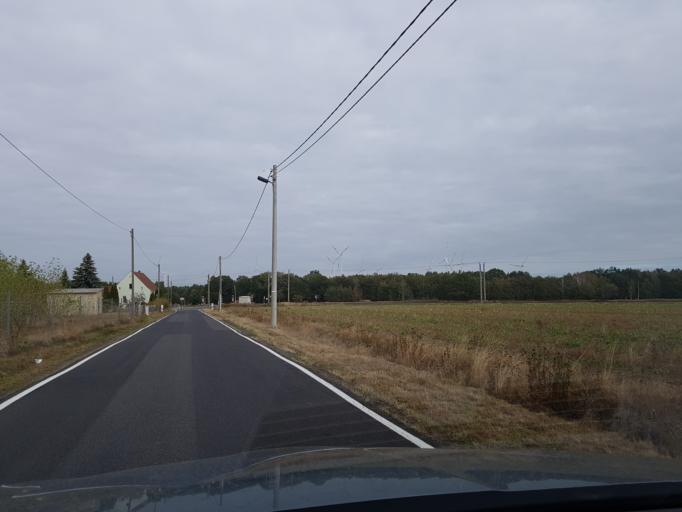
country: DE
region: Brandenburg
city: Falkenberg
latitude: 51.5552
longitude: 13.2941
